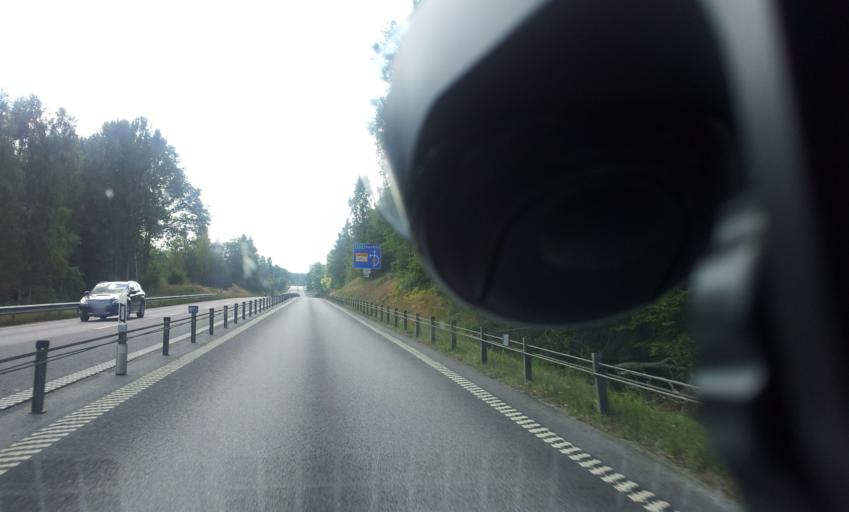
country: SE
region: Kalmar
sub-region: Oskarshamns Kommun
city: Oskarshamn
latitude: 57.3107
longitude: 16.4622
